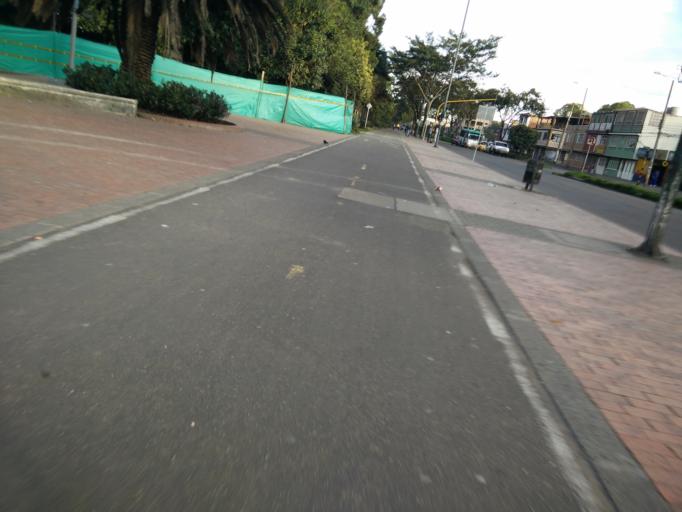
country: CO
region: Bogota D.C.
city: Bogota
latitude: 4.6683
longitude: -74.0971
